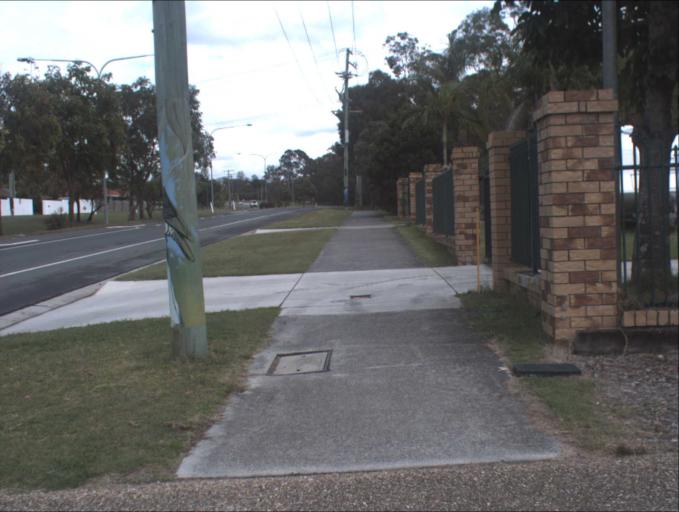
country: AU
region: Queensland
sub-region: Logan
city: Logan Reserve
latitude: -27.6790
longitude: 153.0652
